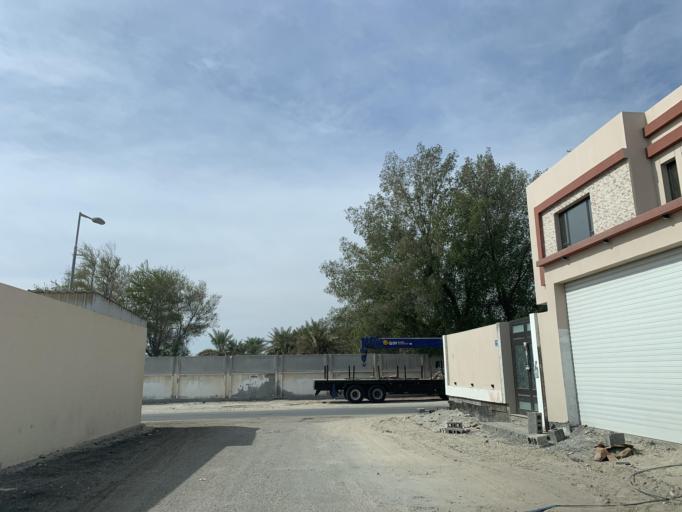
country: BH
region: Central Governorate
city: Madinat Hamad
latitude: 26.1294
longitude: 50.4757
